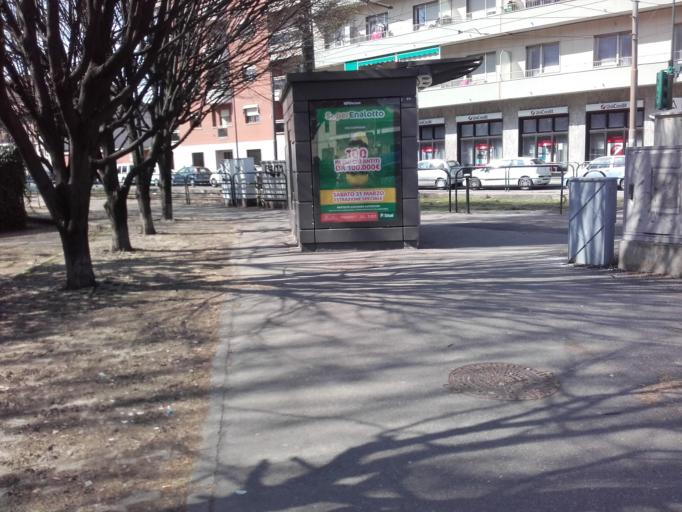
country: IT
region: Piedmont
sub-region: Provincia di Torino
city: Venaria Reale
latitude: 45.1125
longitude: 7.6596
